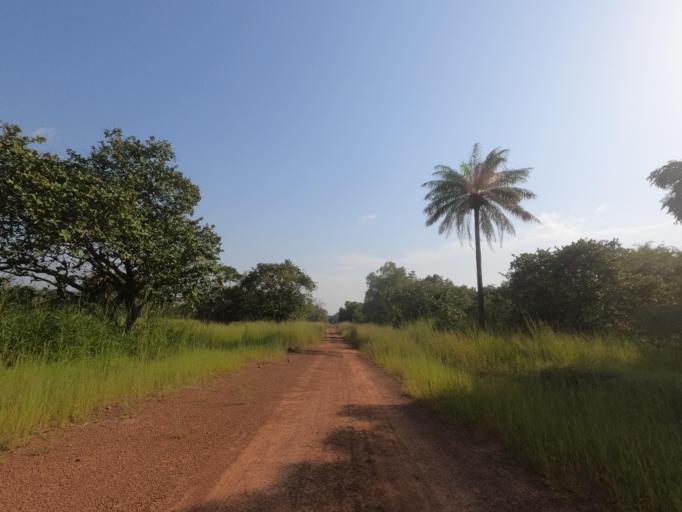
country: SN
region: Sedhiou
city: Sedhiou
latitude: 12.4361
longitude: -15.7380
